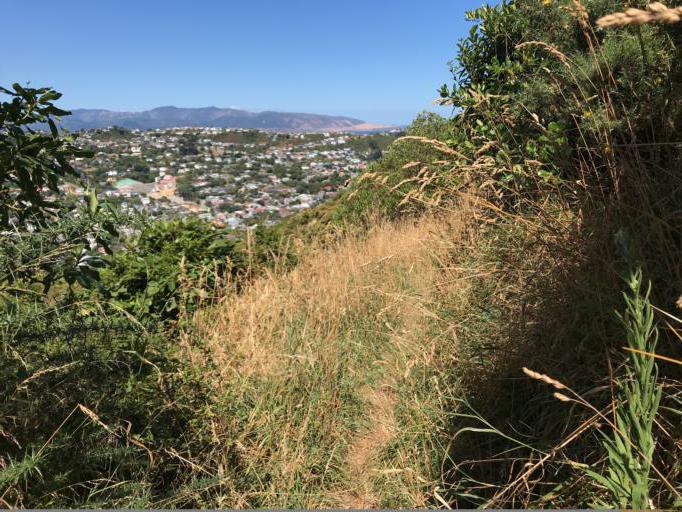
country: NZ
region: Wellington
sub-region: Wellington City
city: Brooklyn
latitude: -41.3299
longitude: 174.7657
